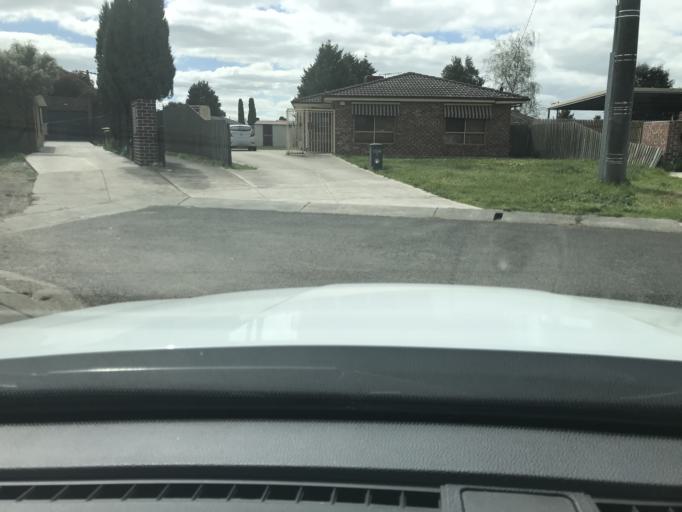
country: AU
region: Victoria
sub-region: Hume
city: Craigieburn
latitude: -37.6109
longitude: 144.9403
